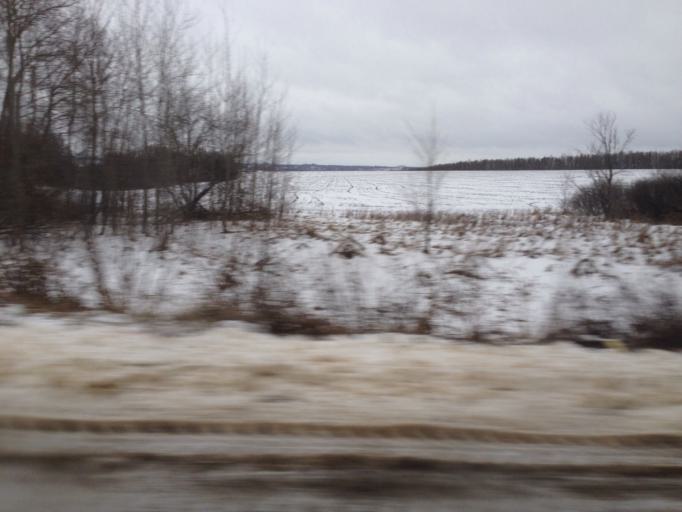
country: RU
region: Tula
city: Bolokhovo
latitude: 54.0431
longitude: 37.8597
